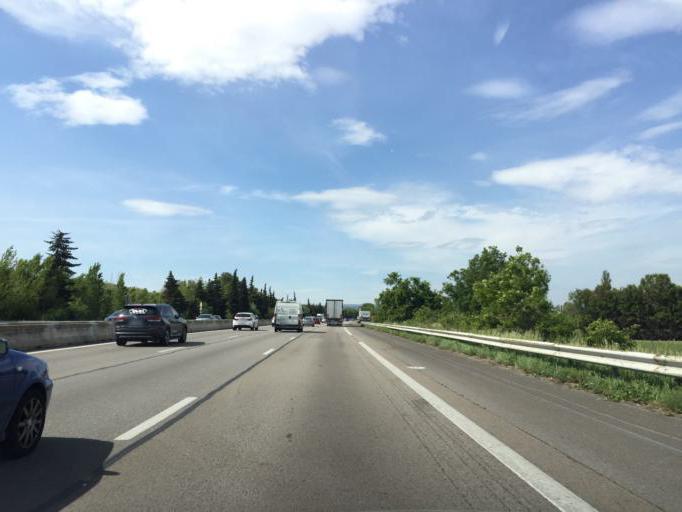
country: FR
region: Rhone-Alpes
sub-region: Departement de la Drome
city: Saulce-sur-Rhone
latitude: 44.6914
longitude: 4.7910
